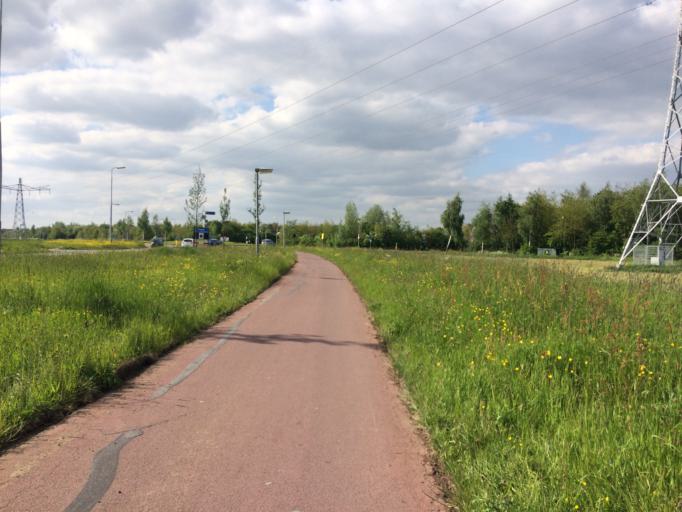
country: NL
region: Gelderland
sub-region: Gemeente Maasdriel
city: Hedel
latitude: 51.7176
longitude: 5.2579
